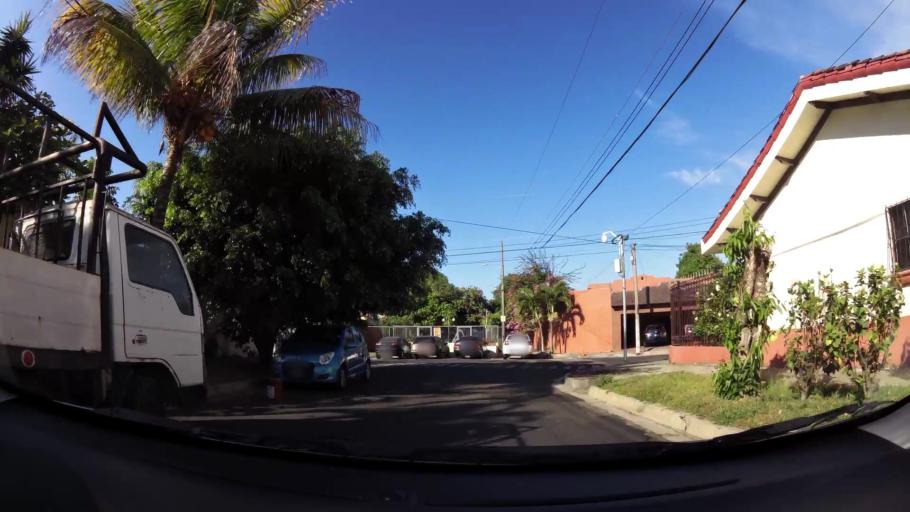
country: SV
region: La Libertad
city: Santa Tecla
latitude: 13.6845
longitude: -89.2904
